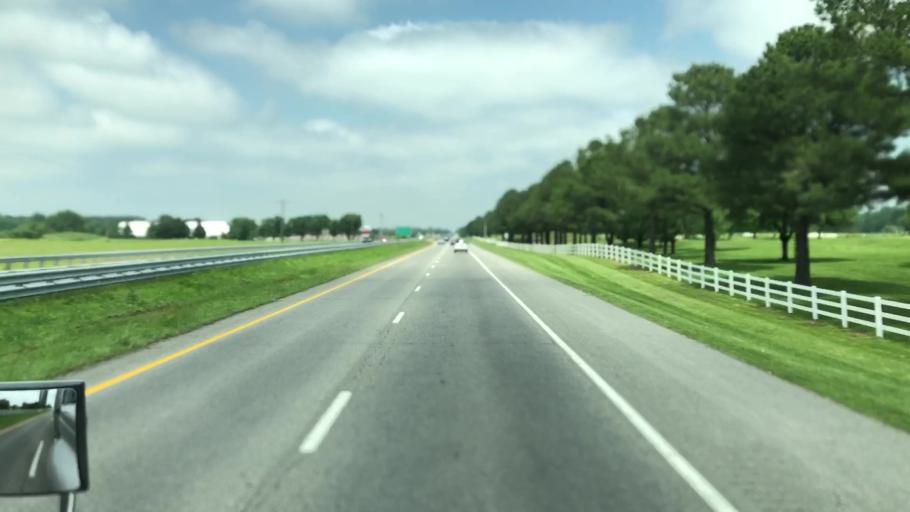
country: US
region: Maryland
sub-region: Talbot County
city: Easton
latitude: 38.8211
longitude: -76.0600
